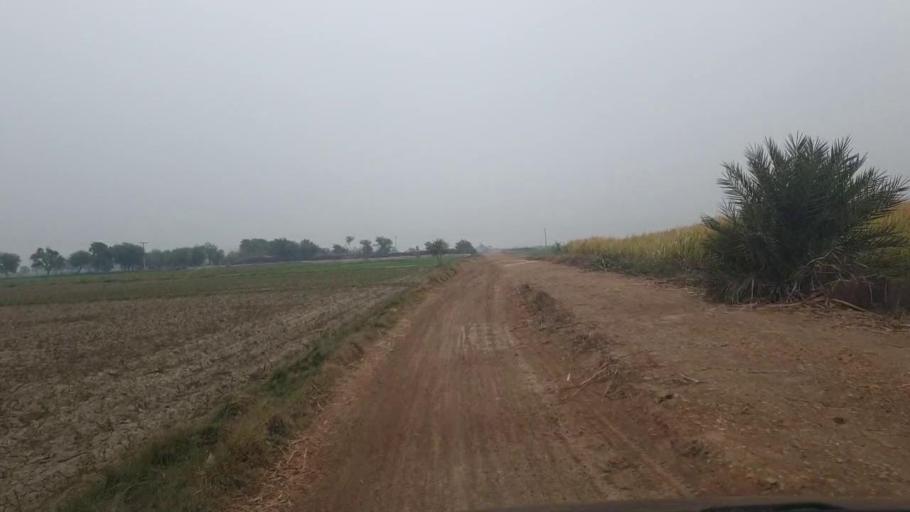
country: PK
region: Sindh
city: Tando Adam
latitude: 25.8028
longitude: 68.6855
